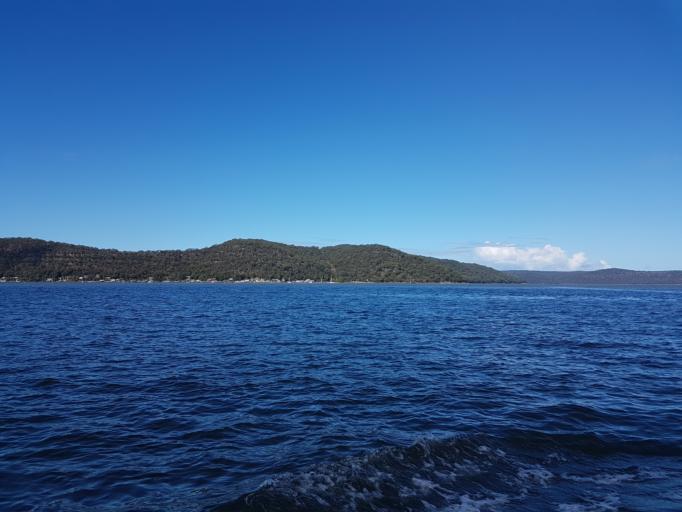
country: AU
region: New South Wales
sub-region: Gosford Shire
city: Umina
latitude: -33.5453
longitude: 151.2325
